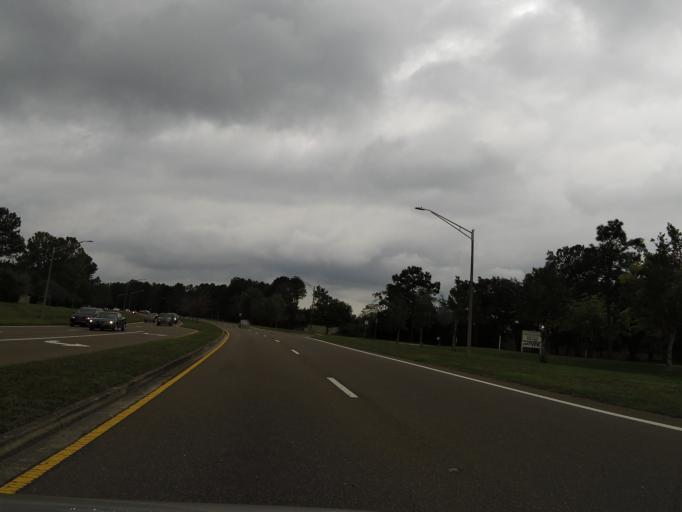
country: US
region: Florida
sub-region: Clay County
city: Bellair-Meadowbrook Terrace
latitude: 30.1982
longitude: -81.7973
